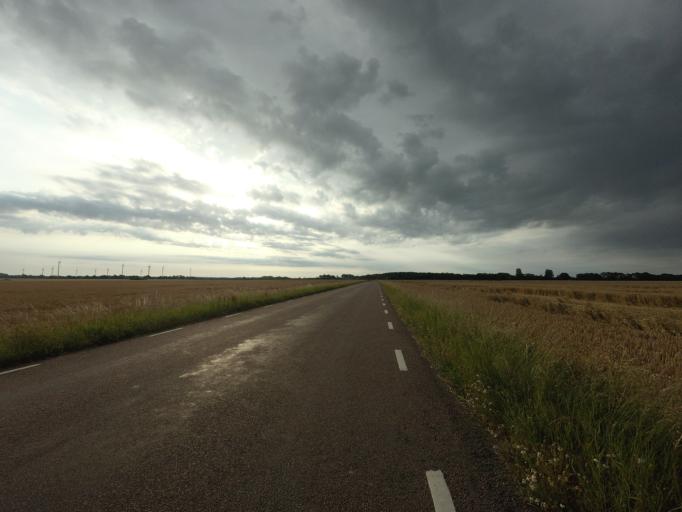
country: SE
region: Skane
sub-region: Helsingborg
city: Odakra
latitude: 56.1548
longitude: 12.7191
